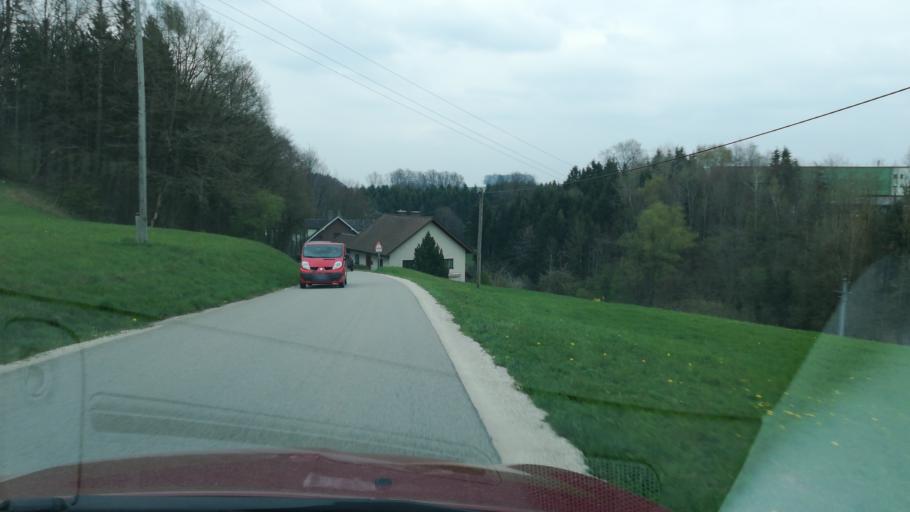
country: AT
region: Upper Austria
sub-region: Politischer Bezirk Vocklabruck
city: Attnang-Puchheim
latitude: 47.9572
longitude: 13.7398
